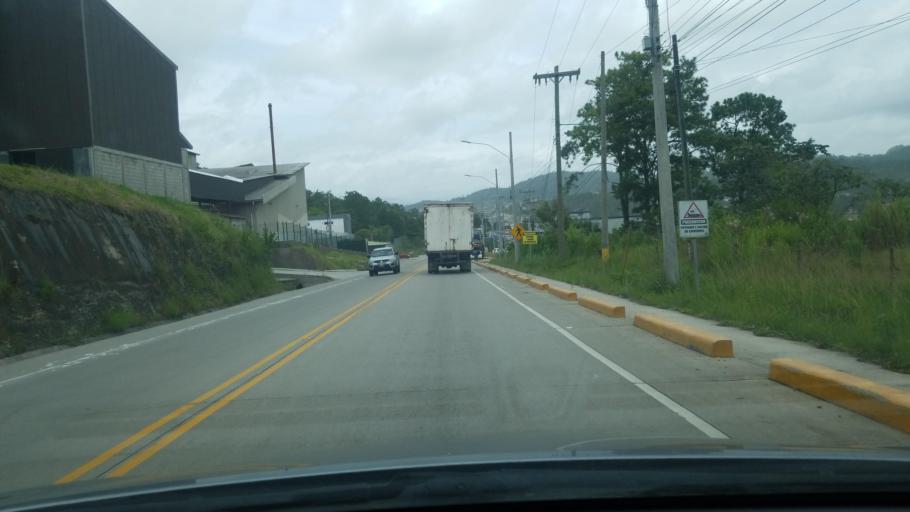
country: HN
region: Copan
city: Santa Rosa de Copan
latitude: 14.7929
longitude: -88.7795
